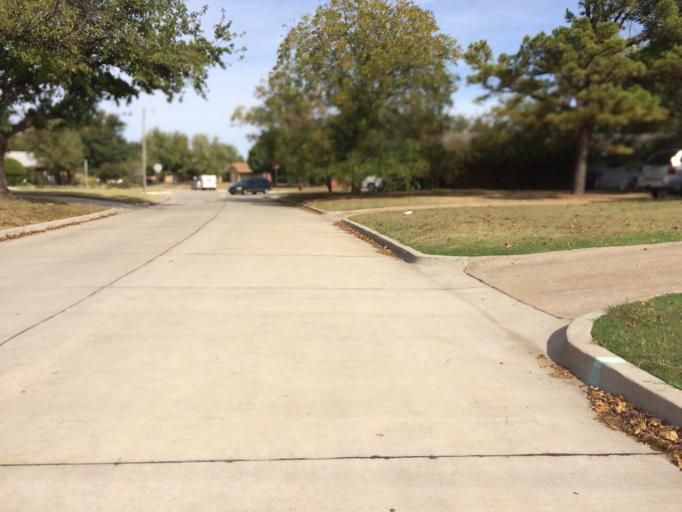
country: US
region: Oklahoma
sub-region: Cleveland County
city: Norman
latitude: 35.2366
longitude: -97.4425
